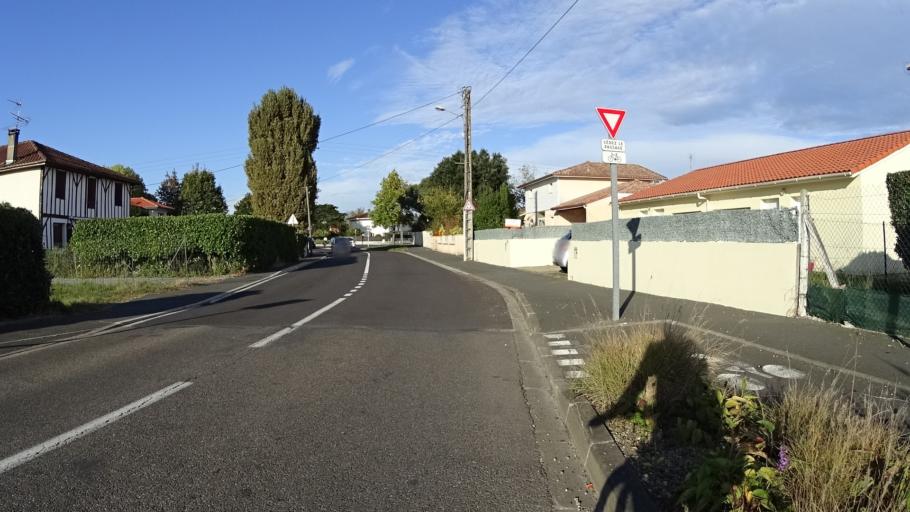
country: FR
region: Aquitaine
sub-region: Departement des Landes
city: Saint-Paul-les-Dax
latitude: 43.7346
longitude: -1.0545
